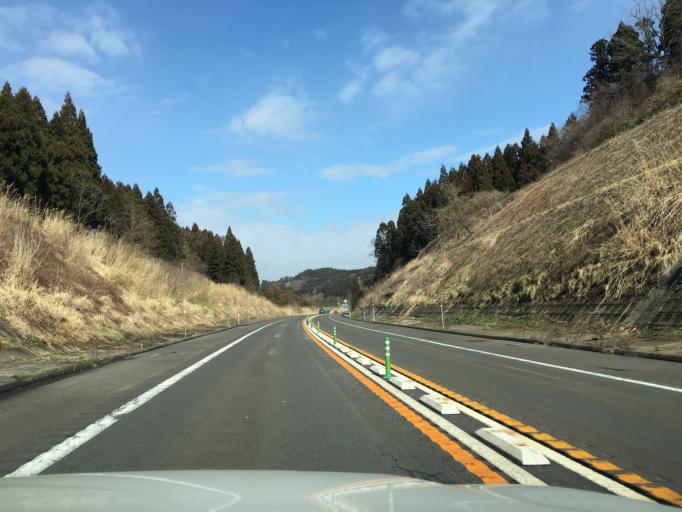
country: JP
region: Akita
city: Akita
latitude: 39.7685
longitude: 140.1218
